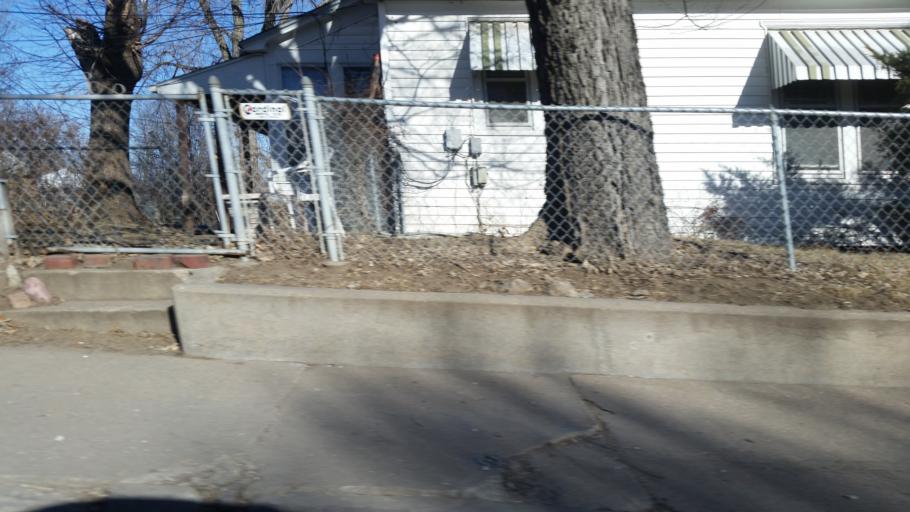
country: US
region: Nebraska
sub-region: Douglas County
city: Omaha
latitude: 41.1922
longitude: -95.9335
